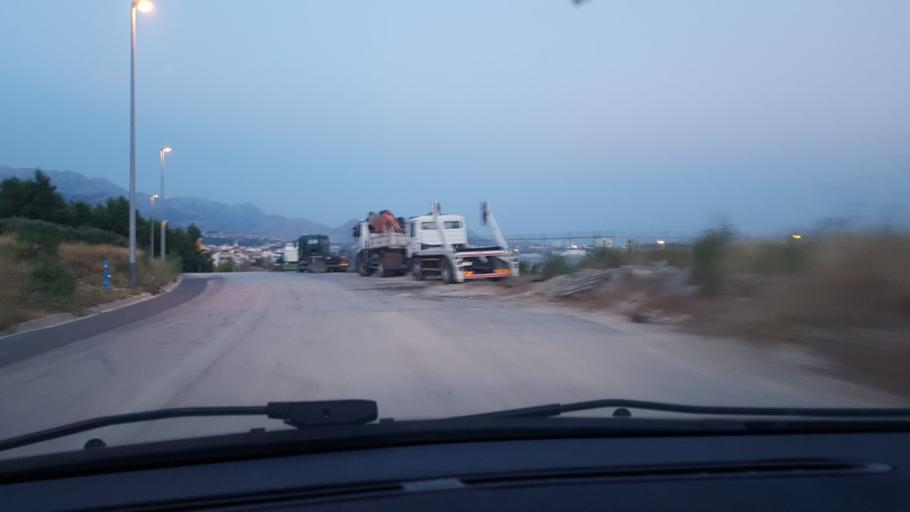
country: HR
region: Splitsko-Dalmatinska
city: Vranjic
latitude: 43.5459
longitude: 16.4548
